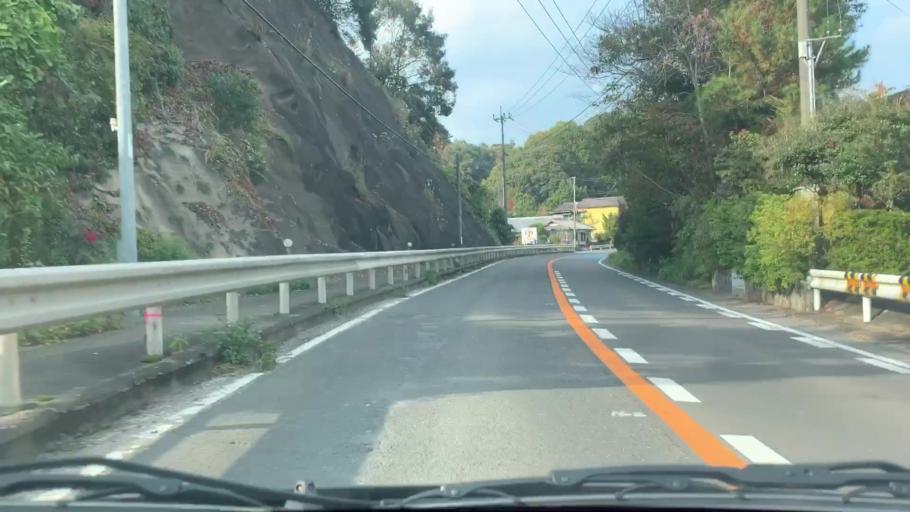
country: JP
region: Nagasaki
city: Sasebo
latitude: 32.9889
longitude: 129.7380
